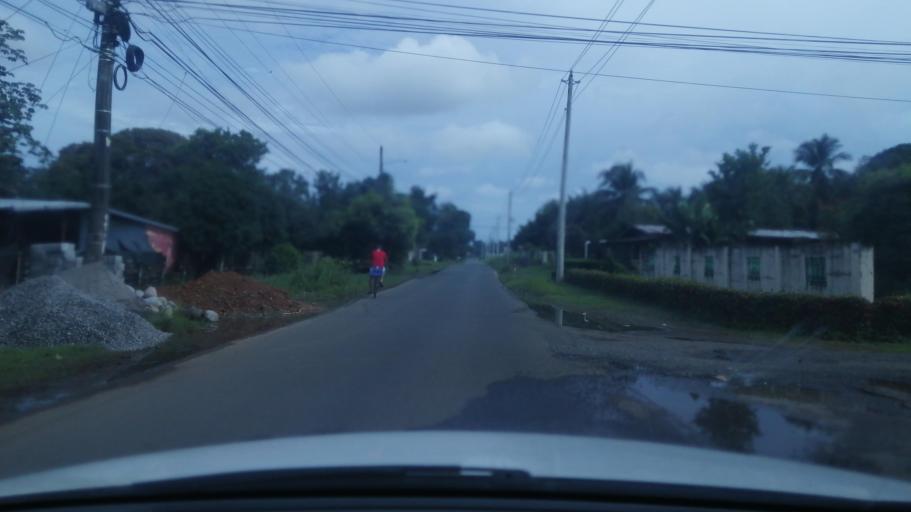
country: PA
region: Chiriqui
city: David
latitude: 8.4087
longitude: -82.4272
